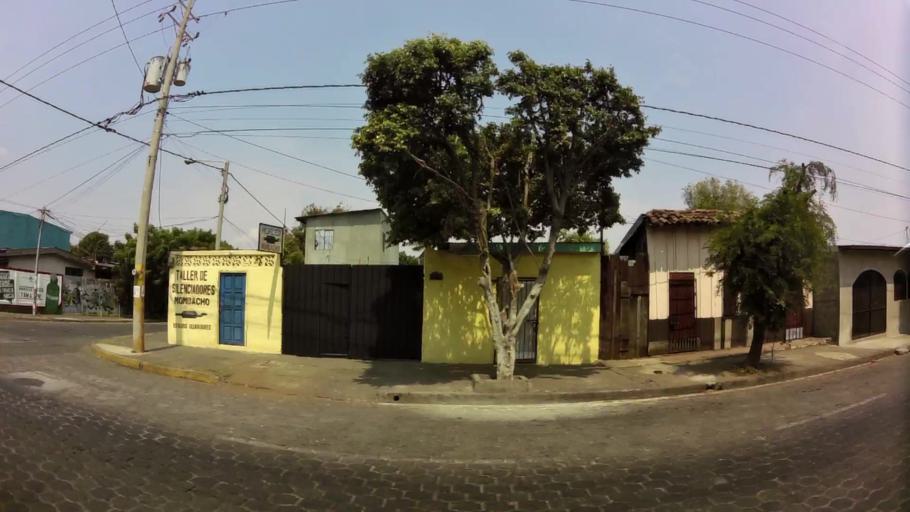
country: NI
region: Managua
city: Ciudad Sandino
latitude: 12.1554
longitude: -86.2971
